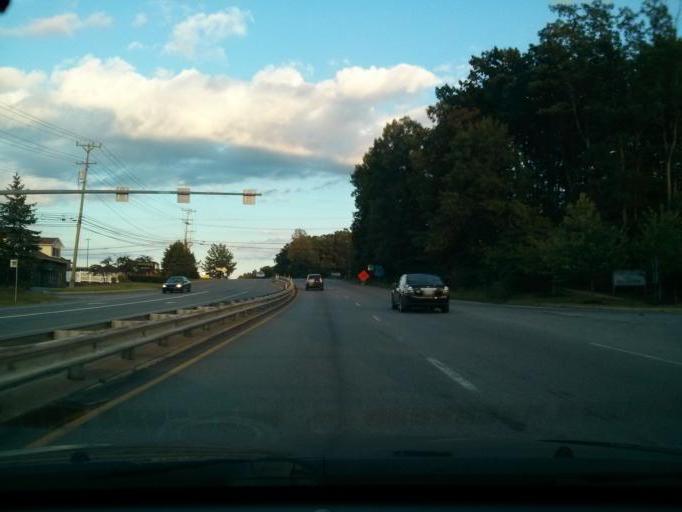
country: US
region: Pennsylvania
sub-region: Centre County
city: Park Forest Village
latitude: 40.8118
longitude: -77.9219
